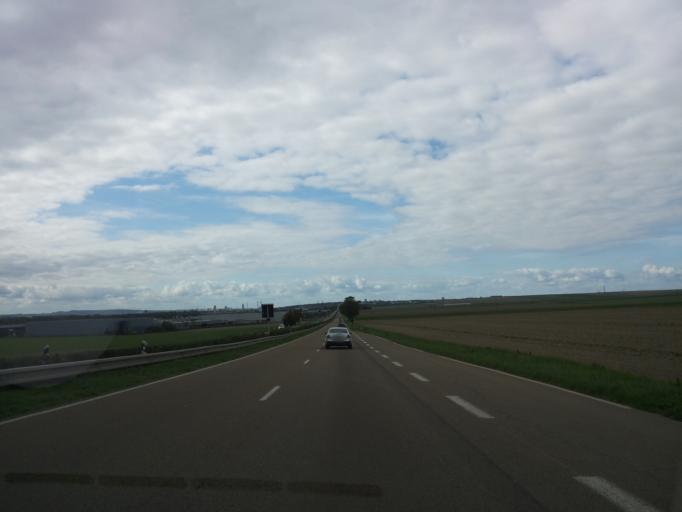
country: FR
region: Champagne-Ardenne
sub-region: Departement de la Marne
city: Sillery
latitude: 49.2181
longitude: 4.1306
